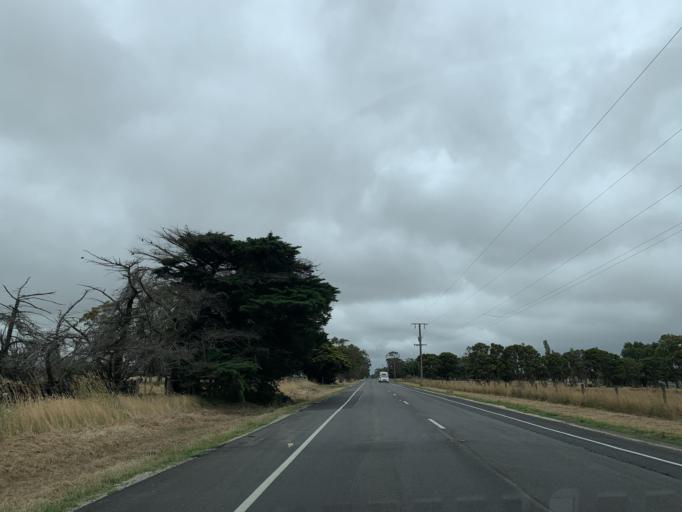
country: AU
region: Victoria
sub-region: Cardinia
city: Officer South
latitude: -38.1410
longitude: 145.3840
